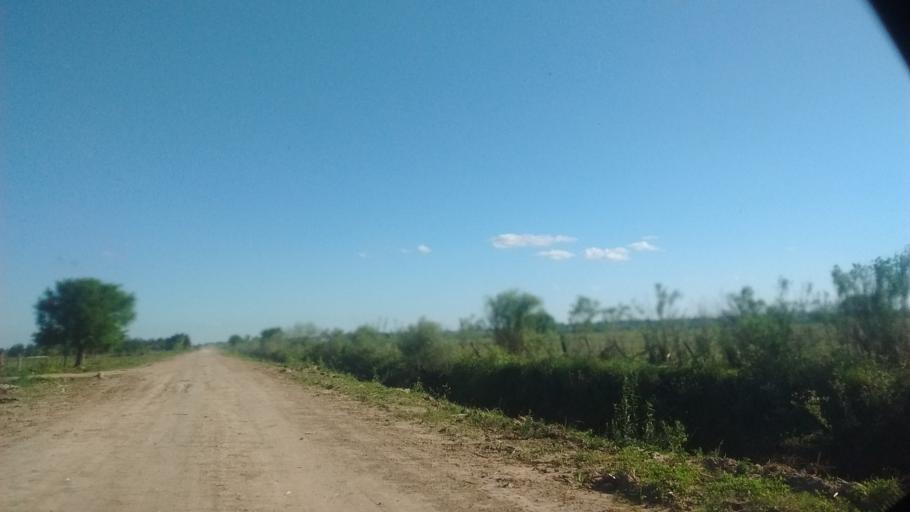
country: AR
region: Santa Fe
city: Funes
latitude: -32.8884
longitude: -60.7978
